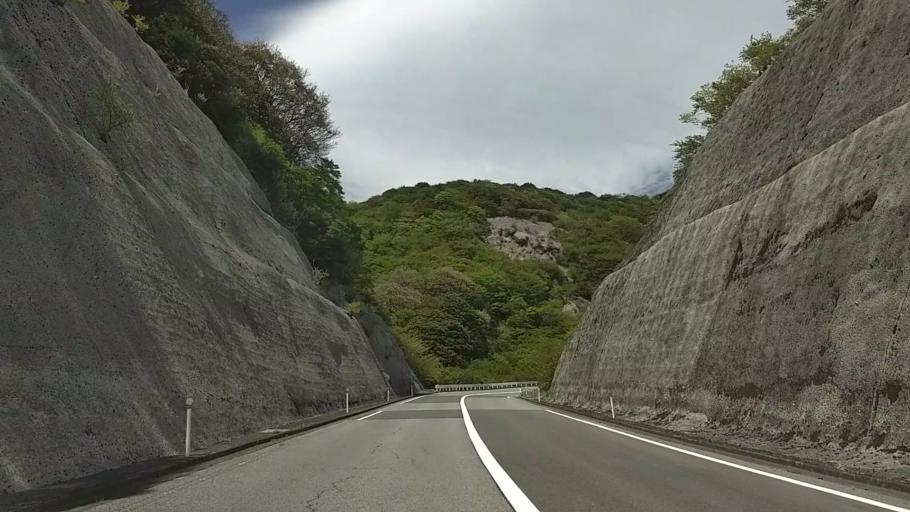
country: JP
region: Kanagawa
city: Hakone
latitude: 35.1729
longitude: 139.0288
